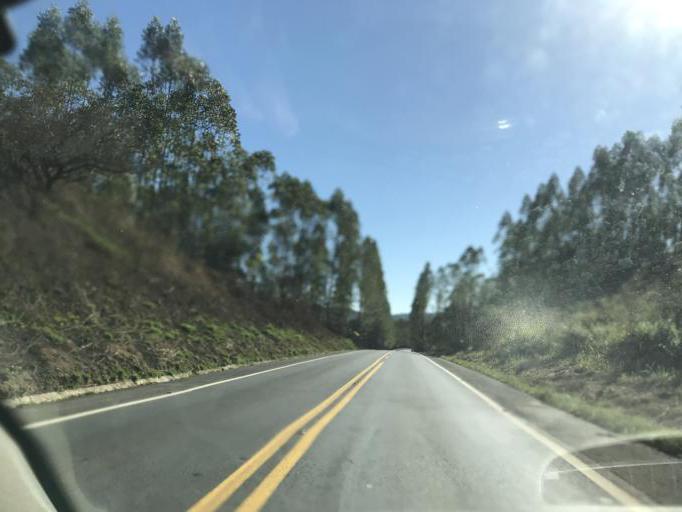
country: BR
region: Minas Gerais
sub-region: Bambui
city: Bambui
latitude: -19.8231
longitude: -46.0140
